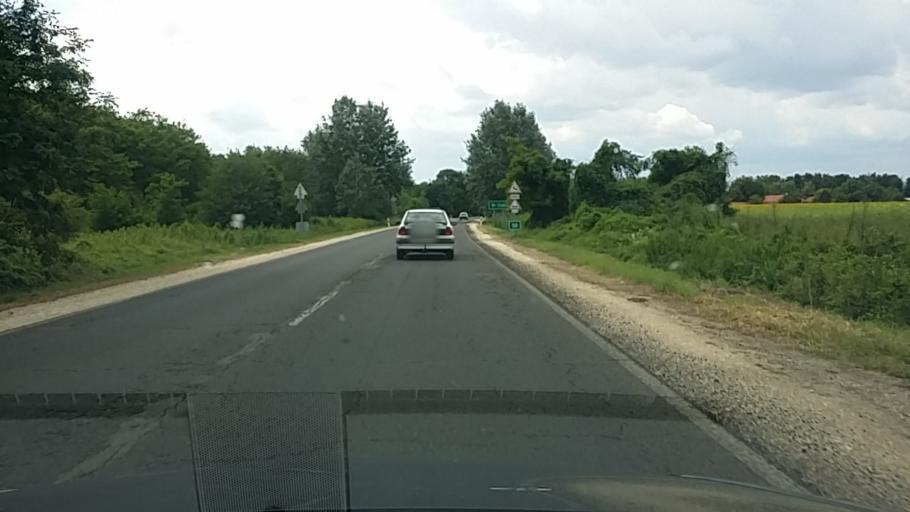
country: HU
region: Pest
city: Hernad
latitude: 47.1470
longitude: 19.3939
